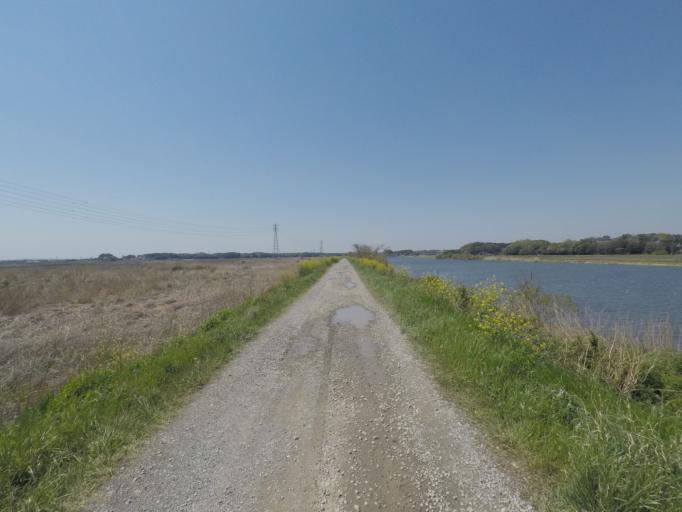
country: JP
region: Ibaraki
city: Ushiku
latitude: 35.9463
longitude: 140.1167
